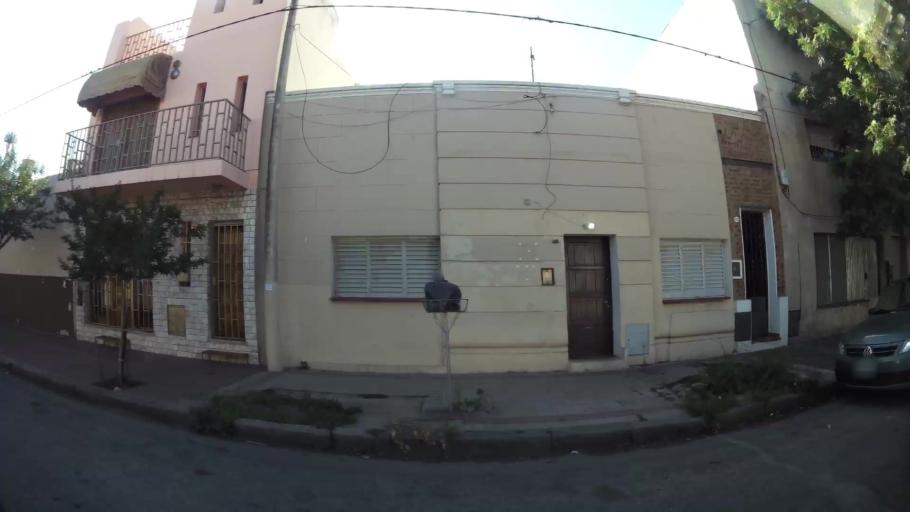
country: AR
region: Cordoba
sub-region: Departamento de Capital
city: Cordoba
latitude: -31.3962
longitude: -64.1746
